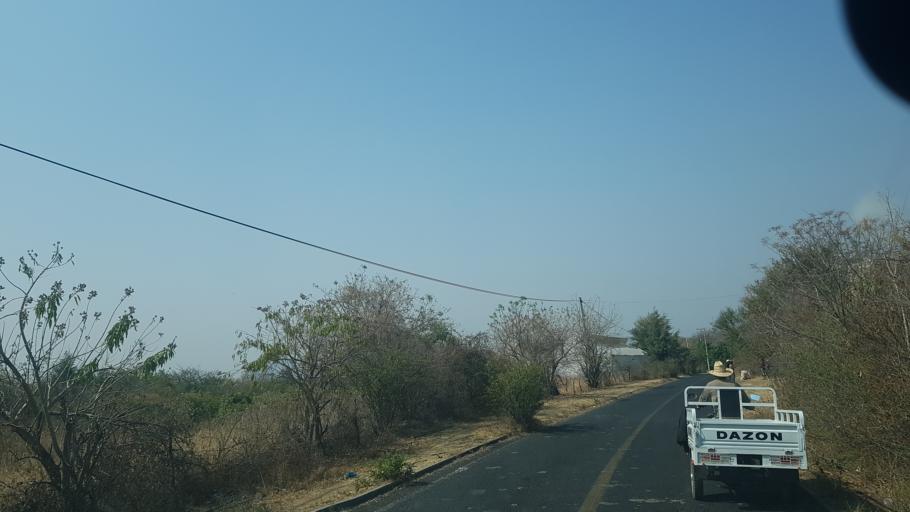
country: MX
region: Morelos
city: Tlacotepec
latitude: 18.8236
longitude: -98.7418
